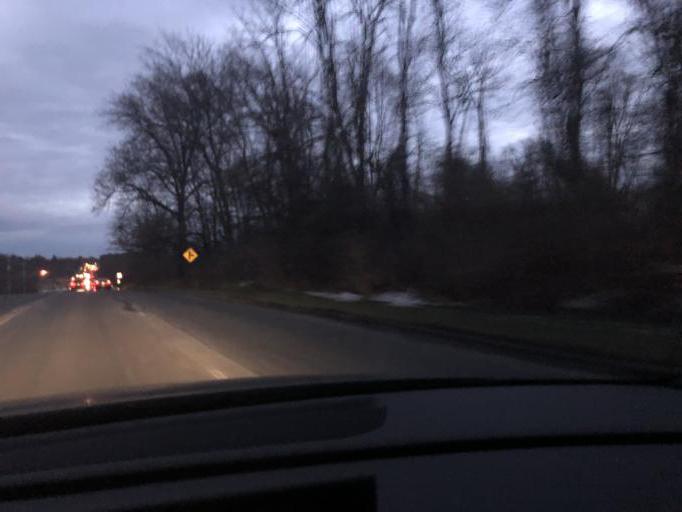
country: US
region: New Jersey
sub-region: Morris County
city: Florham Park
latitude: 40.7902
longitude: -74.4088
